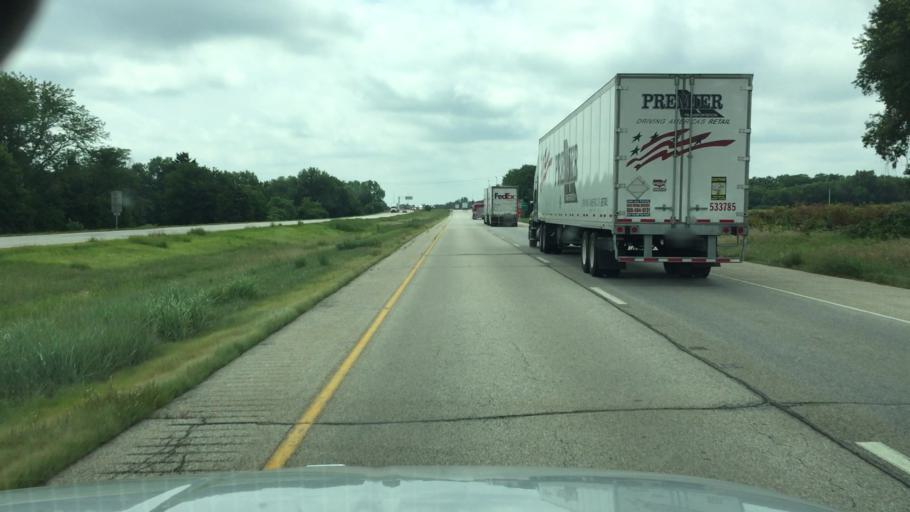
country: US
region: Illinois
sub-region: Knox County
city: Galesburg
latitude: 40.9534
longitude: -90.3329
